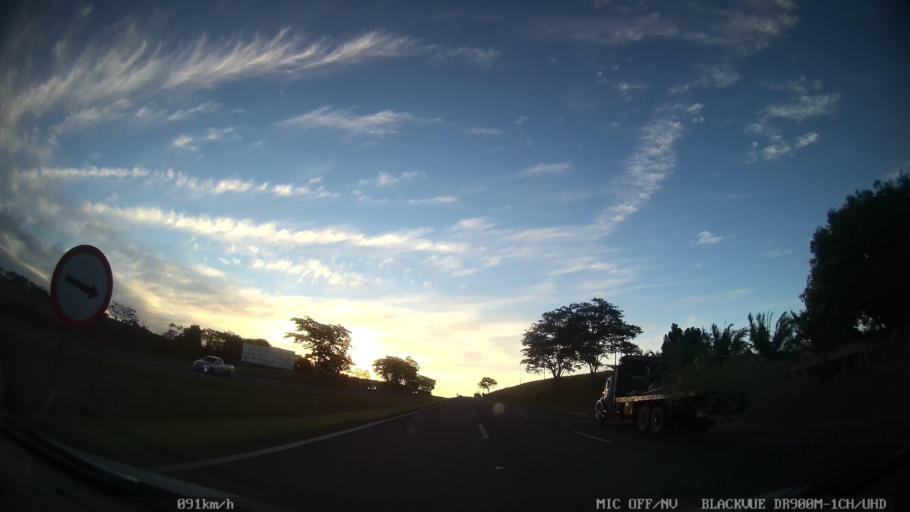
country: BR
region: Sao Paulo
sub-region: Pindorama
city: Pindorama
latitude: -21.2161
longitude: -48.9238
